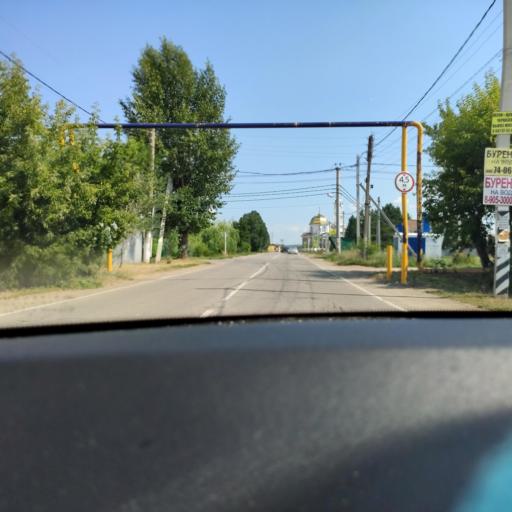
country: RU
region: Samara
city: Volzhskiy
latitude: 53.4498
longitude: 50.1754
